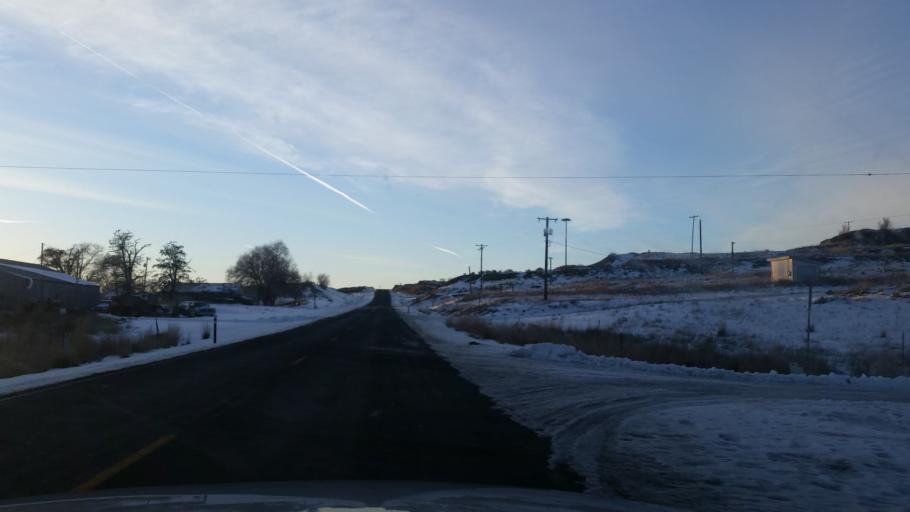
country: US
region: Washington
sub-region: Spokane County
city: Cheney
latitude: 47.1170
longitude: -117.7324
